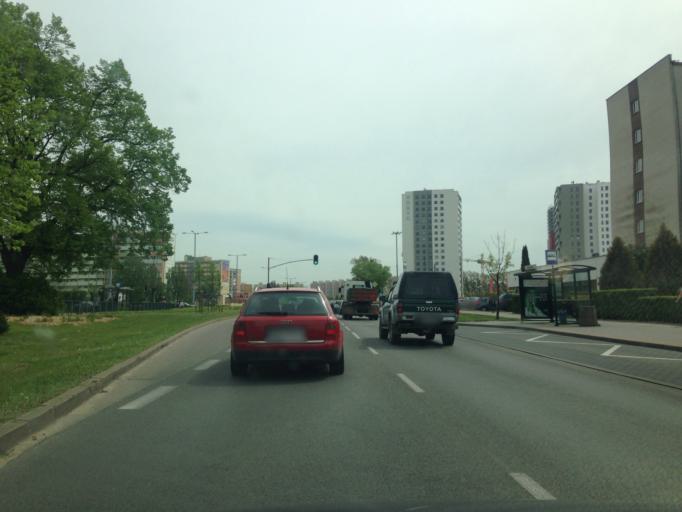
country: PL
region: Pomeranian Voivodeship
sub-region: Sopot
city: Sopot
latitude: 54.4049
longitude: 18.5903
